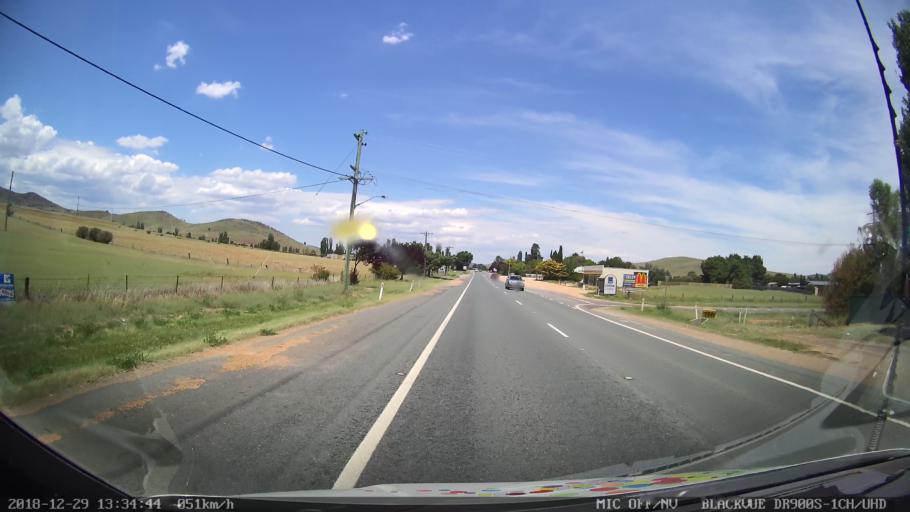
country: AU
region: New South Wales
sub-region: Cooma-Monaro
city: Cooma
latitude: -35.9549
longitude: 149.1476
